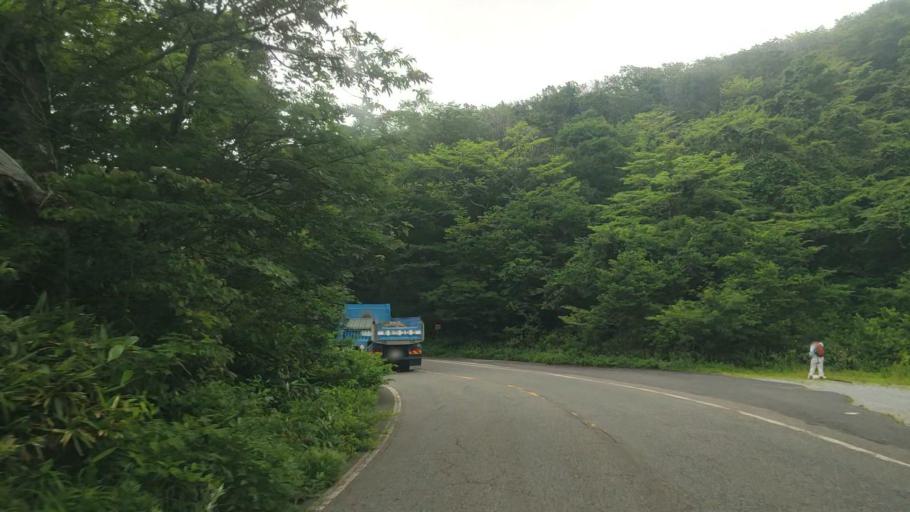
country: JP
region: Tottori
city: Yonago
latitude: 35.3781
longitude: 133.5205
